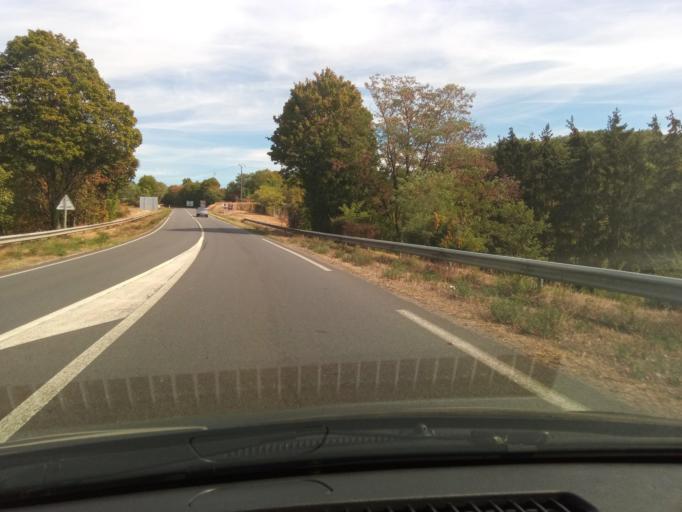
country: FR
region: Poitou-Charentes
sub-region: Departement de la Vienne
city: Chauvigny
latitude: 46.5579
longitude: 0.6422
